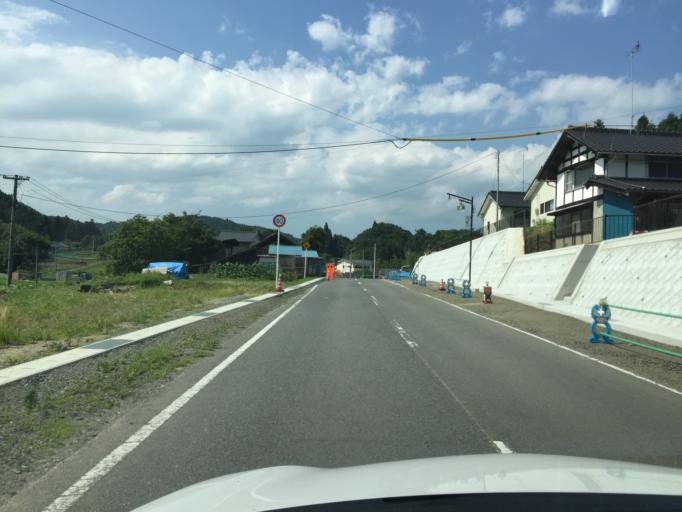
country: JP
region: Ibaraki
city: Kitaibaraki
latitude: 36.9609
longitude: 140.7038
